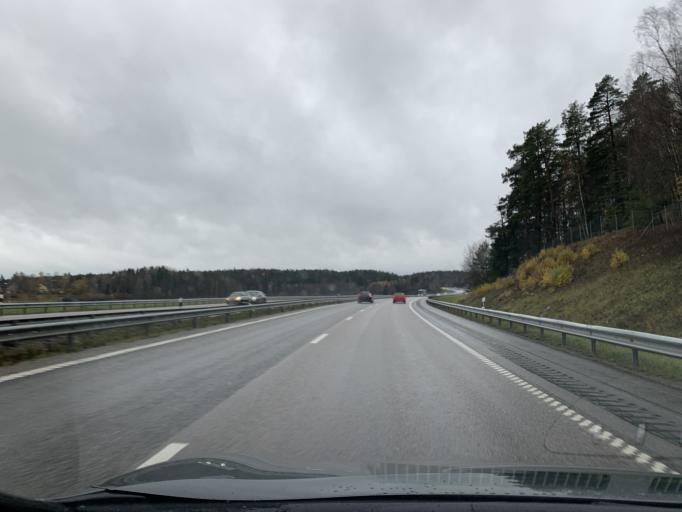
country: SE
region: Stockholm
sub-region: Sodertalje Kommun
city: Pershagen
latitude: 59.1201
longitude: 17.6265
